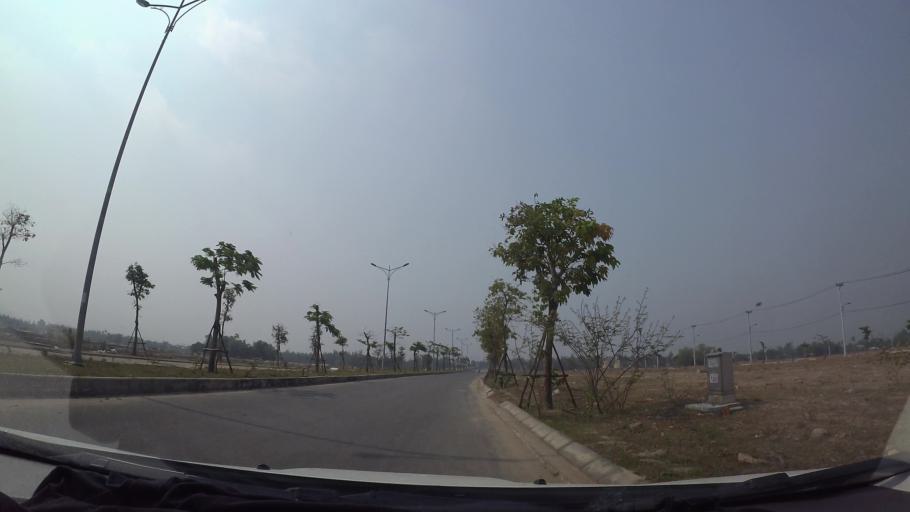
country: VN
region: Da Nang
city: Ngu Hanh Son
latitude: 15.9975
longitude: 108.2476
